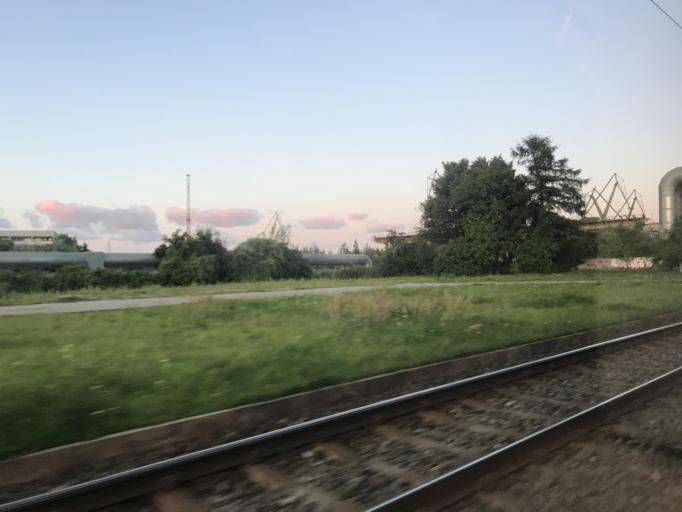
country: PL
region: Pomeranian Voivodeship
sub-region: Gdansk
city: Gdansk
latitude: 54.3700
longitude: 18.6364
